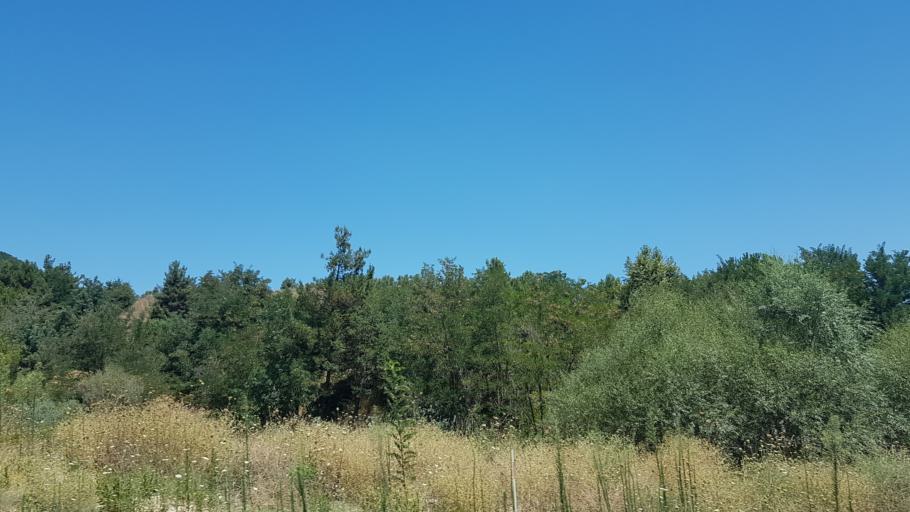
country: TR
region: Mugla
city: Yatagan
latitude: 37.3187
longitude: 28.0799
